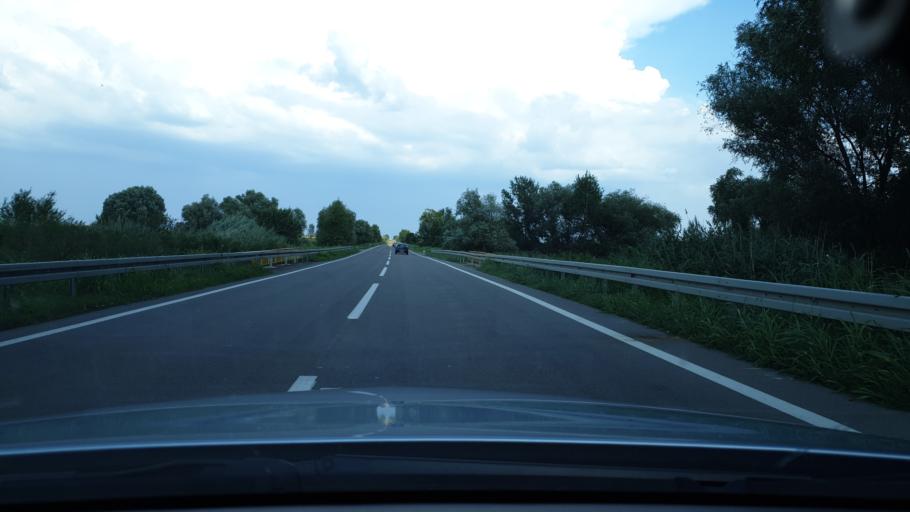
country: RS
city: Aradac
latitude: 45.3879
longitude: 20.2460
